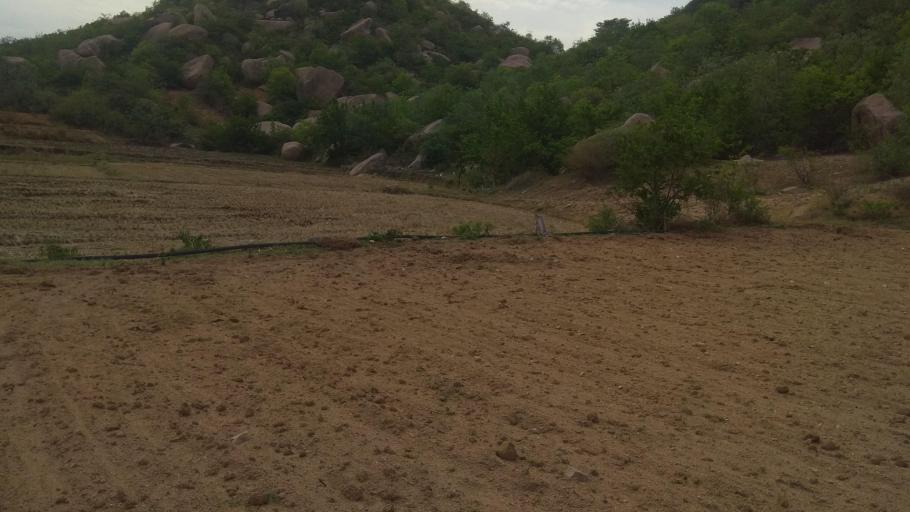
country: IN
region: Telangana
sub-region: Mahbubnagar
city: Farrukhnagar
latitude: 16.8910
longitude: 78.4926
